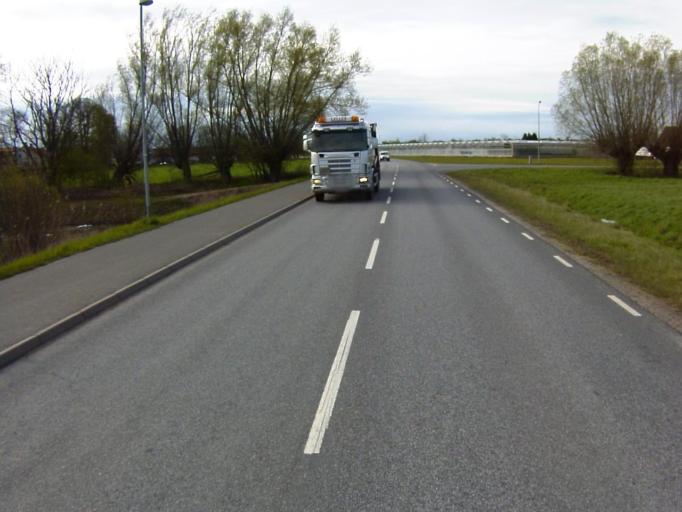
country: SE
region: Skane
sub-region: Kristianstads Kommun
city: Kristianstad
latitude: 56.0123
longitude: 14.1252
